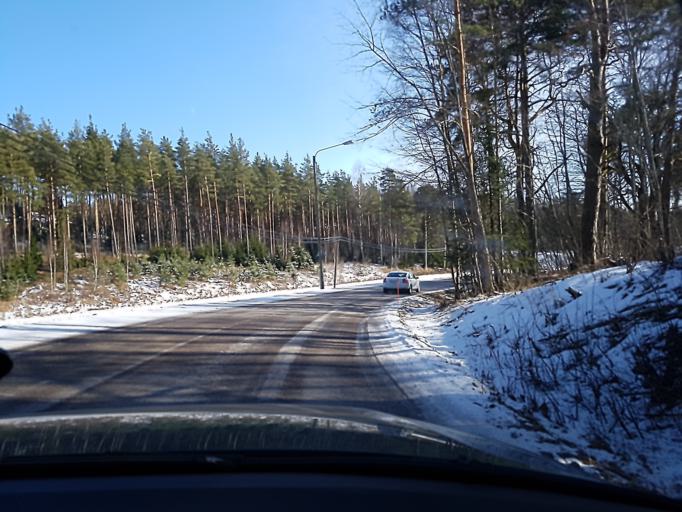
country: FI
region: Uusimaa
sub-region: Helsinki
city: Siuntio
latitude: 60.0999
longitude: 24.3007
